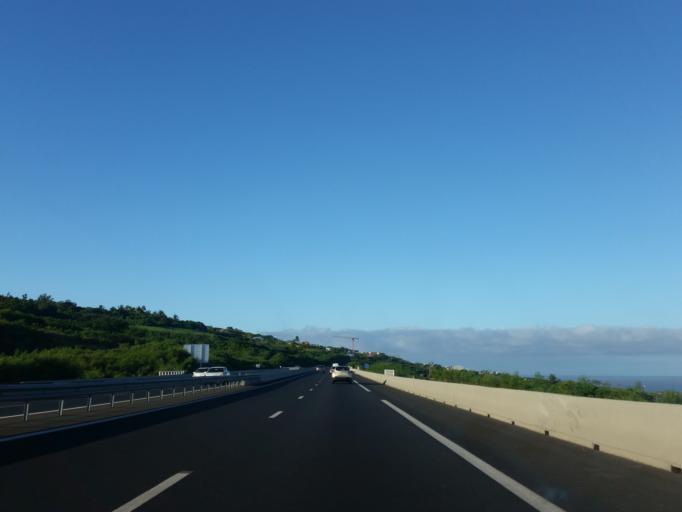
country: RE
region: Reunion
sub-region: Reunion
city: Saint-Leu
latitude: -21.1820
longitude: 55.2963
